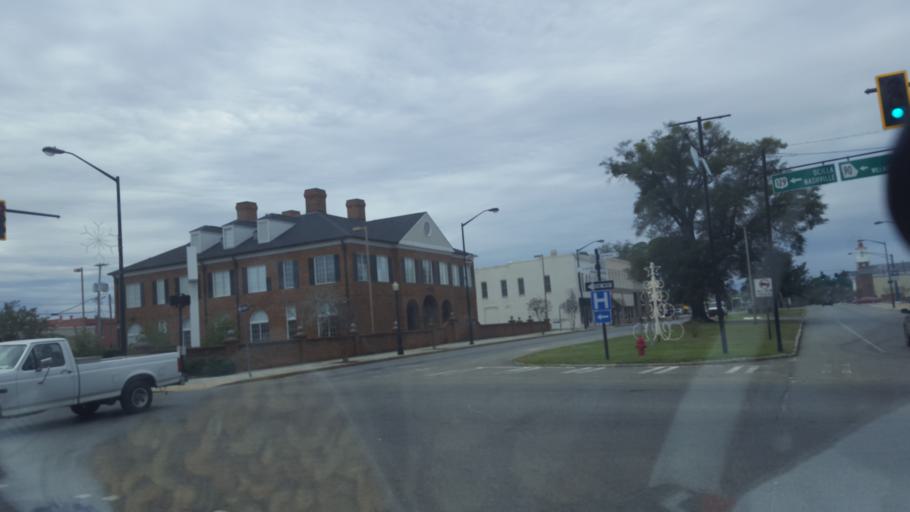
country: US
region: Georgia
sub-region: Ben Hill County
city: Fitzgerald
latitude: 31.7149
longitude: -83.2528
